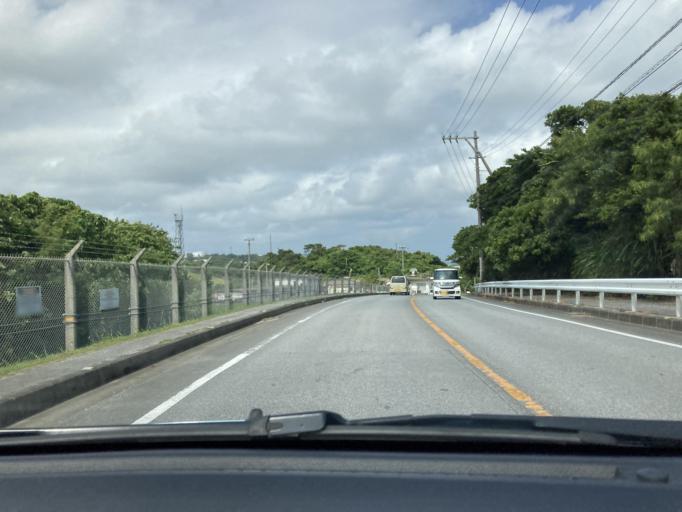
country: JP
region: Okinawa
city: Ishikawa
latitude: 26.4019
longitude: 127.8459
